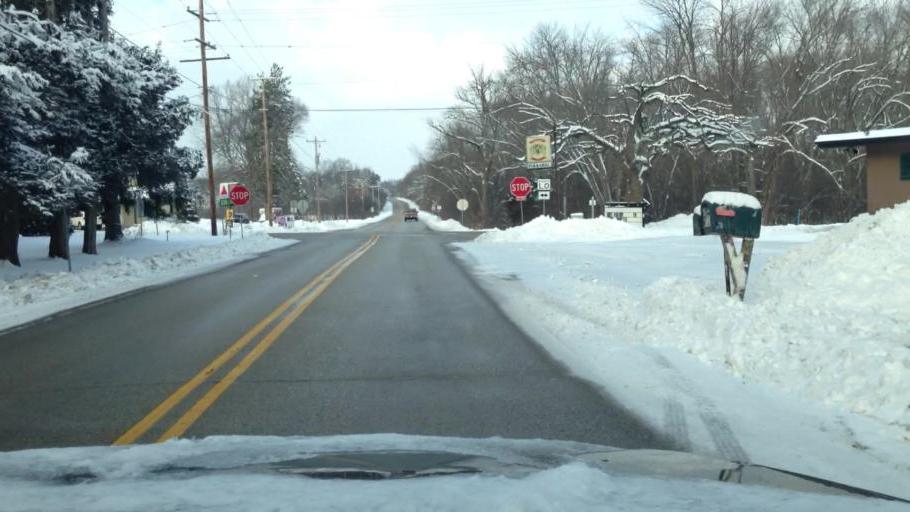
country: US
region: Wisconsin
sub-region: Waukesha County
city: Eagle
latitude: 42.8579
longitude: -88.4316
